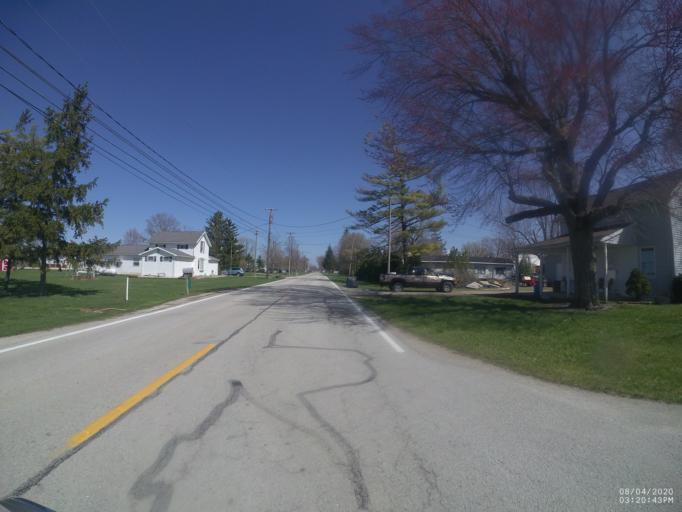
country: US
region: Ohio
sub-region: Sandusky County
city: Stony Prairie
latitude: 41.2677
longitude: -83.2567
